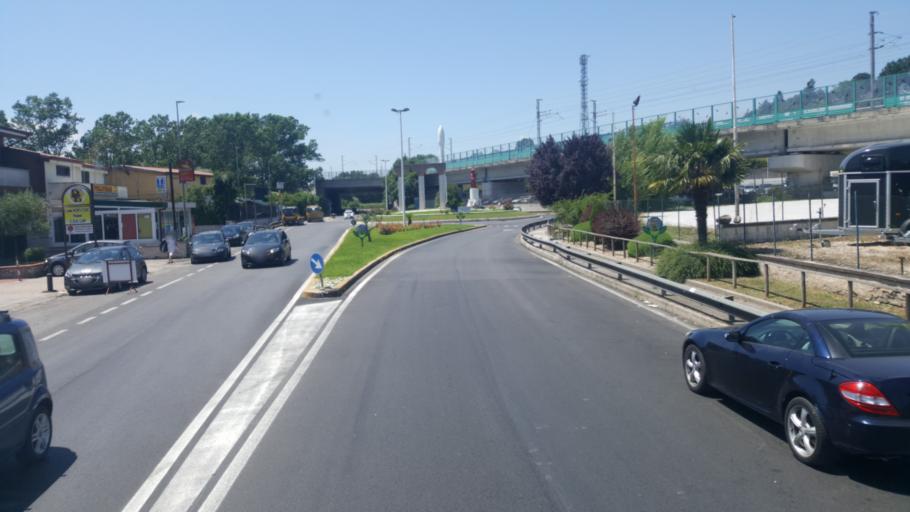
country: IT
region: Latium
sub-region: Citta metropolitana di Roma Capitale
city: Colleferro
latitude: 41.7477
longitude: 12.9928
